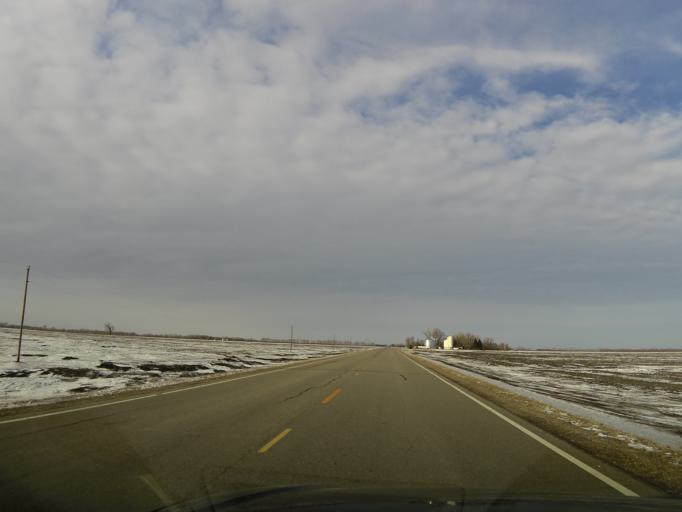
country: US
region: Minnesota
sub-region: Kittson County
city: Hallock
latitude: 48.5520
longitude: -97.1069
